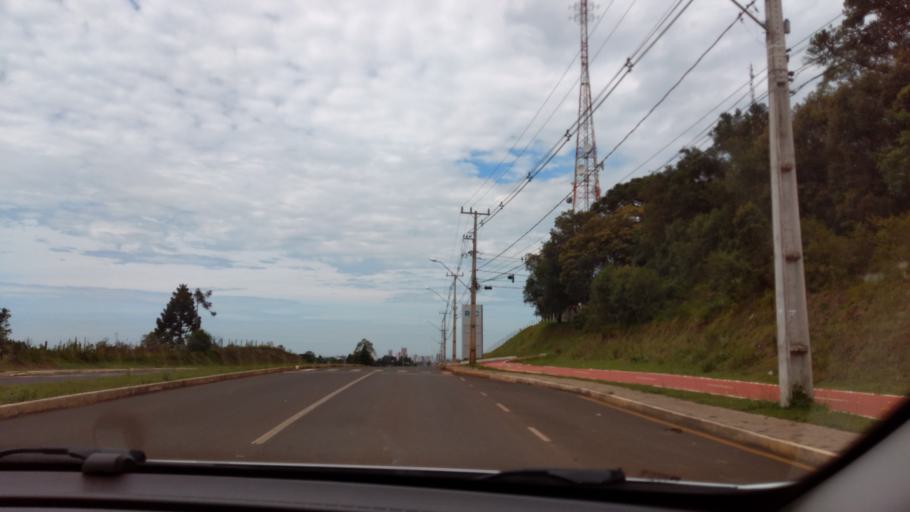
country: BR
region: Parana
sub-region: Guarapuava
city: Guarapuava
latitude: -25.3656
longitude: -51.4342
